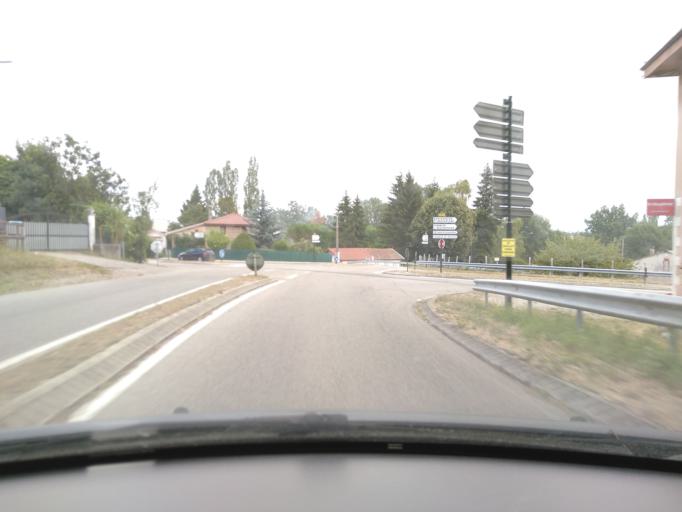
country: FR
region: Rhone-Alpes
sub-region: Departement de l'Isere
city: Saint-Jean-de-Bournay
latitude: 45.4029
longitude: 5.1292
